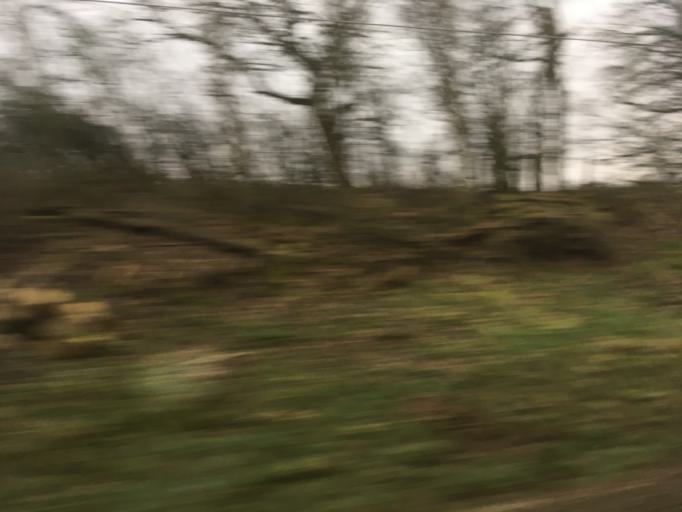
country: GB
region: England
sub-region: Wiltshire
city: Malmesbury
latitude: 51.5417
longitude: -2.1191
